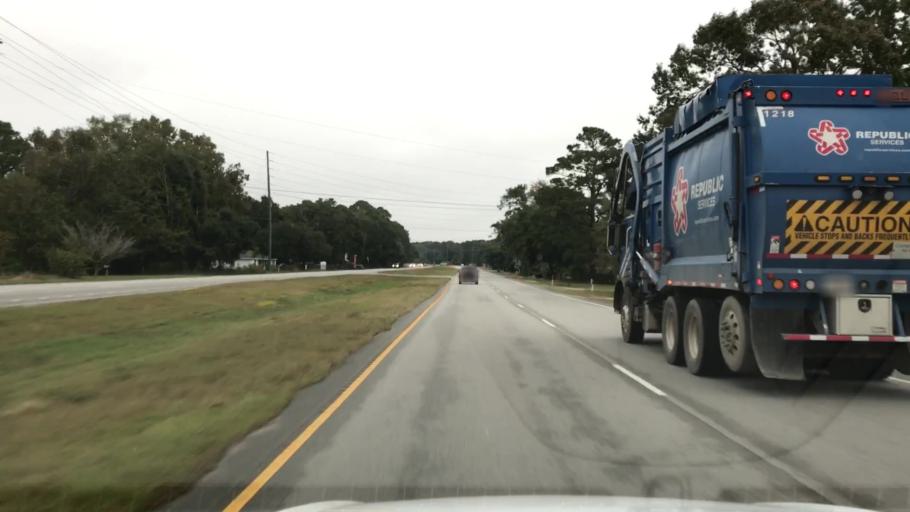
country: US
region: South Carolina
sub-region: Charleston County
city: Isle of Palms
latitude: 32.8851
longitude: -79.7479
